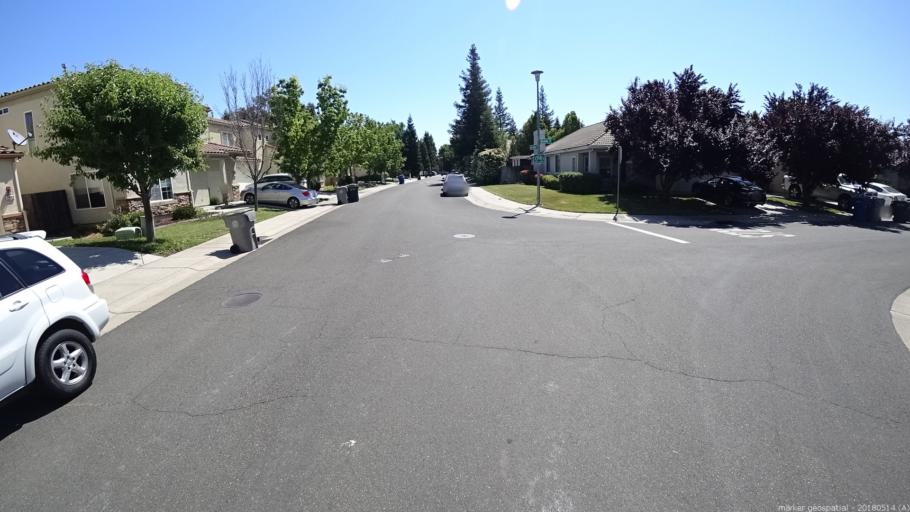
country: US
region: California
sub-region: Yolo County
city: West Sacramento
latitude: 38.6410
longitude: -121.5337
